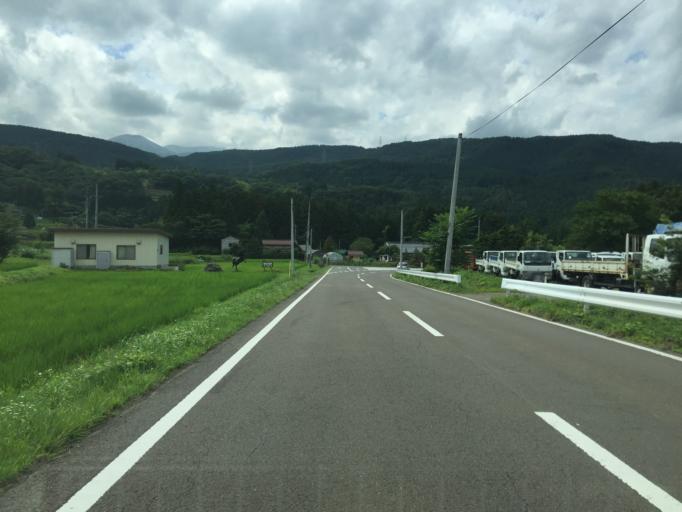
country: JP
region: Fukushima
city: Fukushima-shi
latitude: 37.7115
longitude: 140.3529
